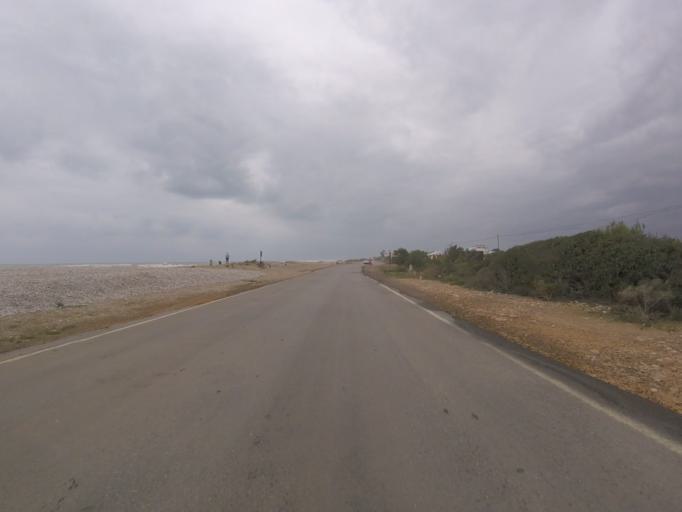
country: ES
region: Valencia
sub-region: Provincia de Castello
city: Alcoceber
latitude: 40.2167
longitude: 0.2669
